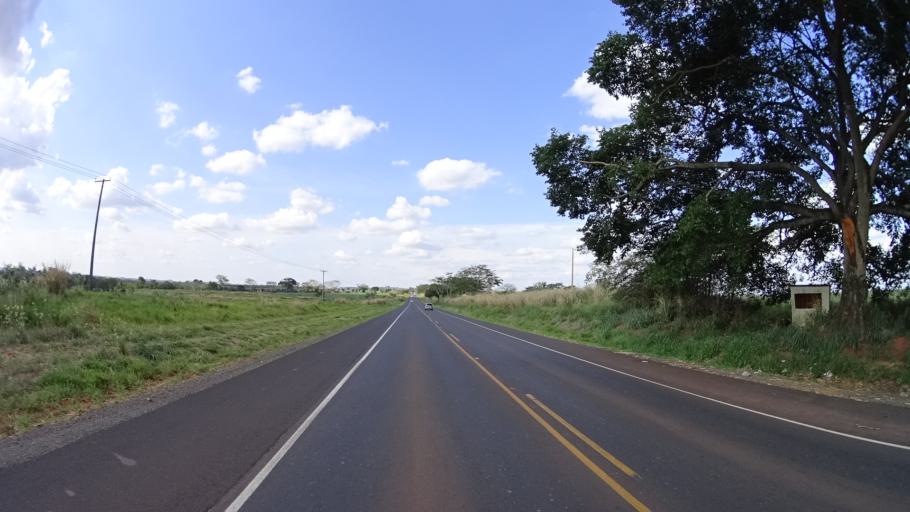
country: BR
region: Sao Paulo
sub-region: Urupes
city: Urupes
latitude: -21.0281
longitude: -49.2360
